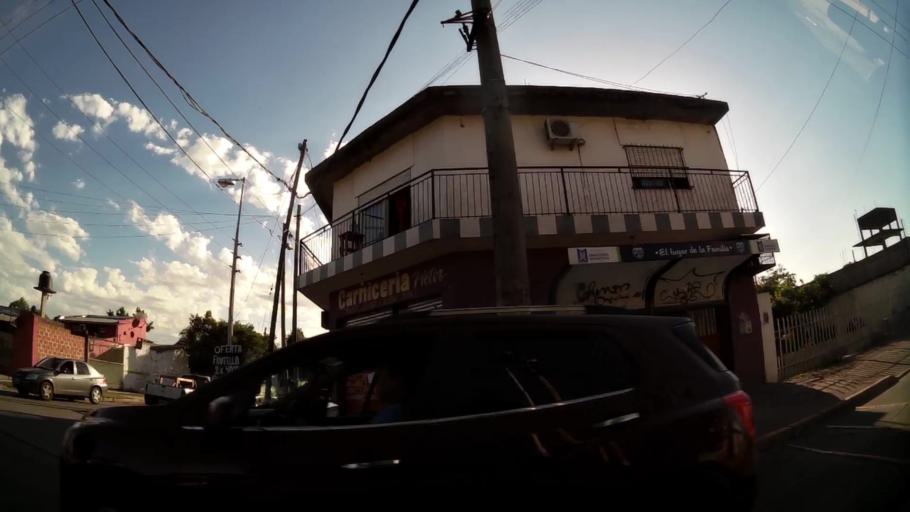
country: AR
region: Buenos Aires
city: Santa Catalina - Dique Lujan
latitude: -34.4988
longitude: -58.7169
